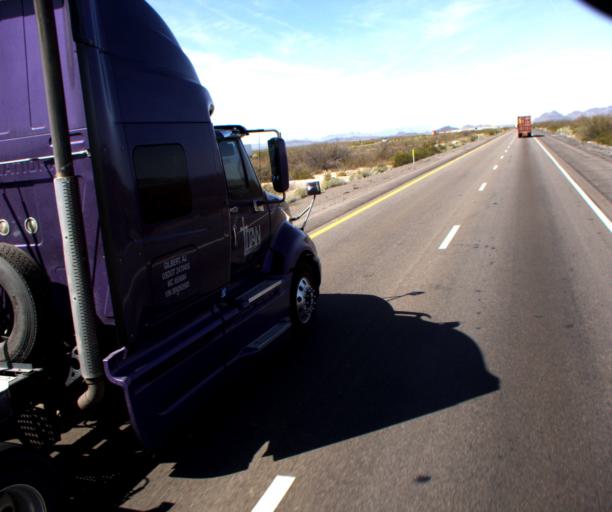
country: US
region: Arizona
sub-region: La Paz County
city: Salome
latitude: 33.5924
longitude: -113.5064
